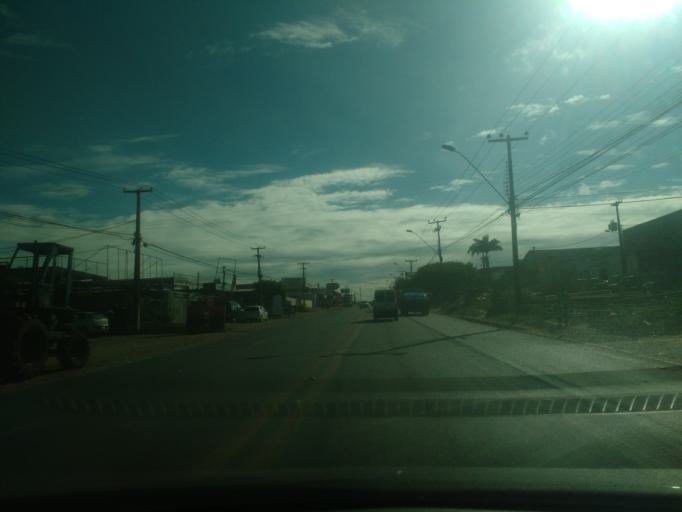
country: BR
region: Alagoas
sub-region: Satuba
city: Satuba
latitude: -9.5628
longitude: -35.7705
